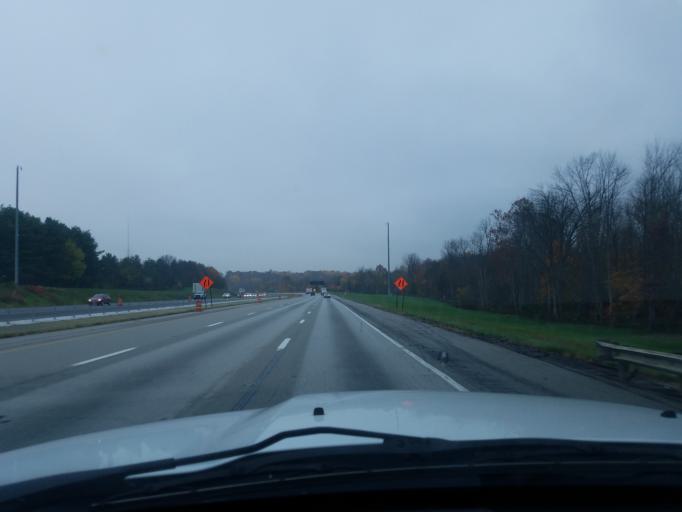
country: US
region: Kentucky
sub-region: Hardin County
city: Elizabethtown
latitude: 37.6933
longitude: -85.8402
